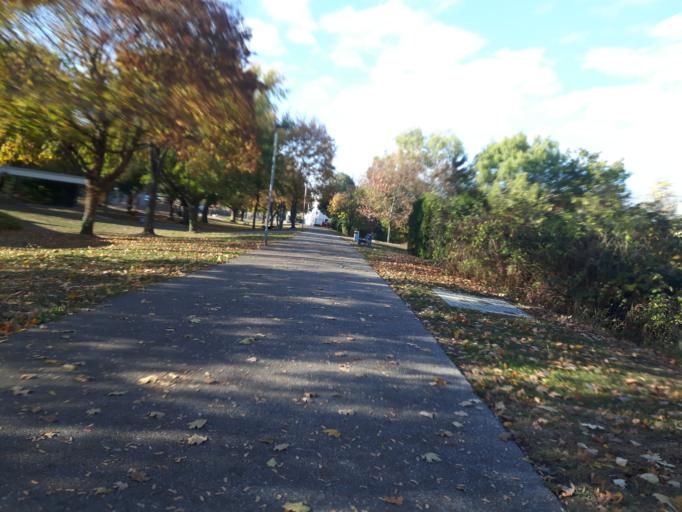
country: DE
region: Baden-Wuerttemberg
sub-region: Karlsruhe Region
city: Sankt Leon-Rot
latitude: 49.2624
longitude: 8.6312
